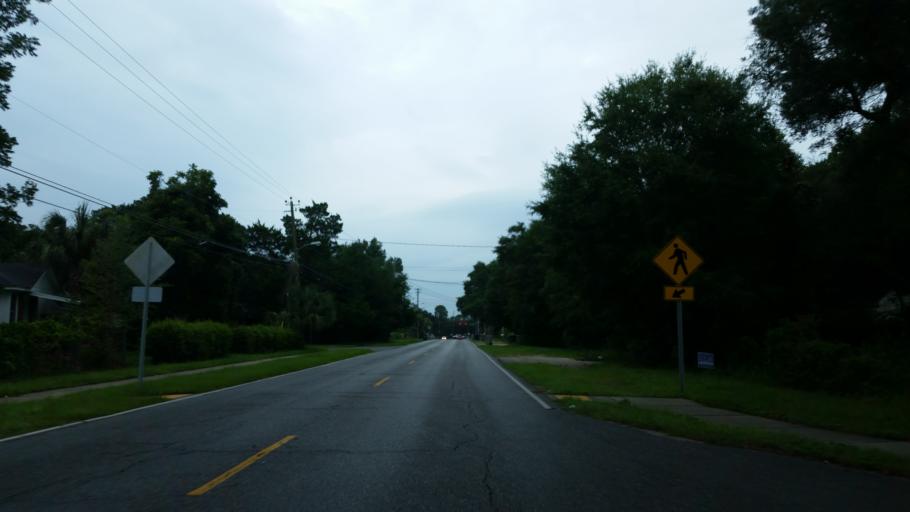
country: US
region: Florida
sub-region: Escambia County
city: Warrington
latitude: 30.3916
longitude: -87.2730
